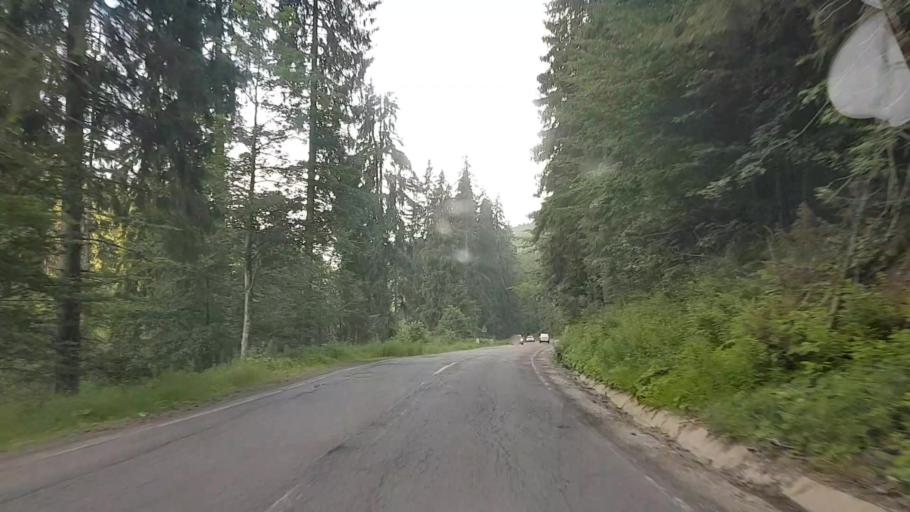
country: RO
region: Harghita
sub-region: Comuna Varsag
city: Varsag
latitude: 46.6398
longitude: 25.2716
